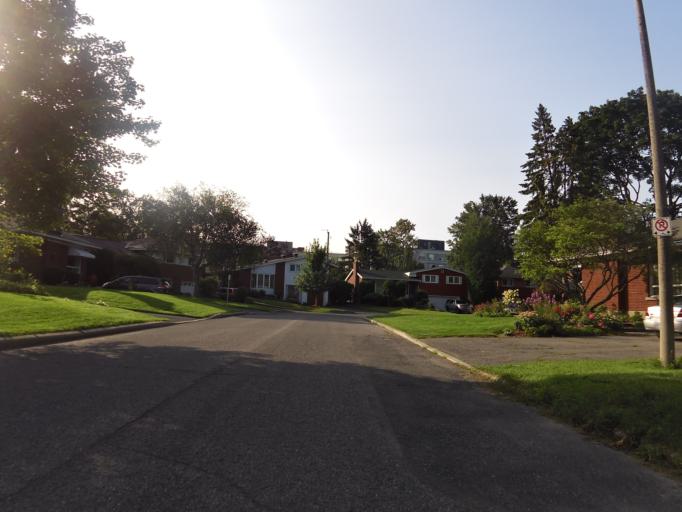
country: CA
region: Ontario
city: Ottawa
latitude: 45.3569
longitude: -75.7552
